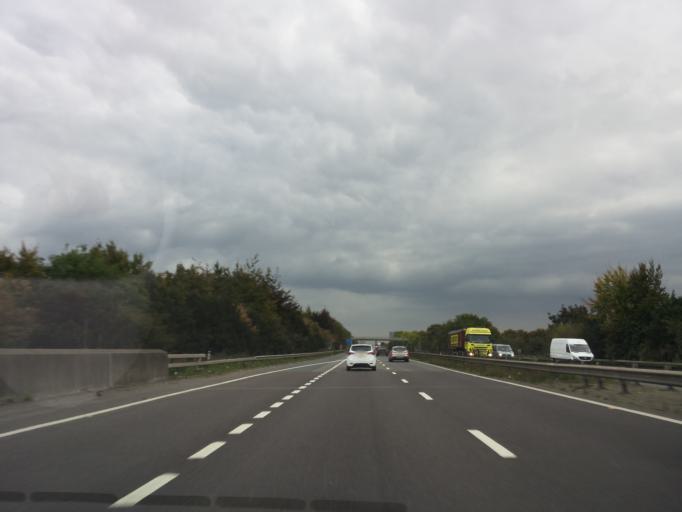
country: GB
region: England
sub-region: Kent
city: Newington
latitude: 51.3293
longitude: 0.6644
